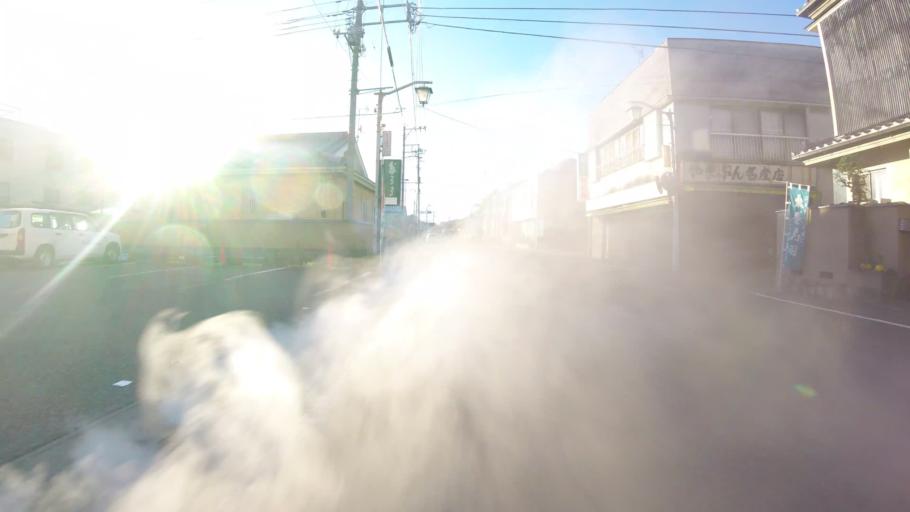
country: JP
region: Shizuoka
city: Mishima
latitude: 35.0359
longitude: 138.9366
